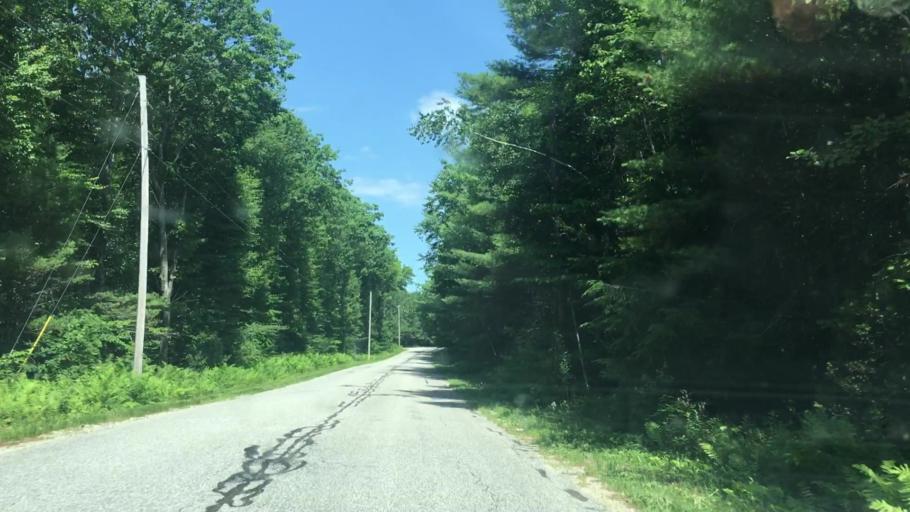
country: US
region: Maine
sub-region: Kennebec County
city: Wayne
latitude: 44.3169
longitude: -70.0582
